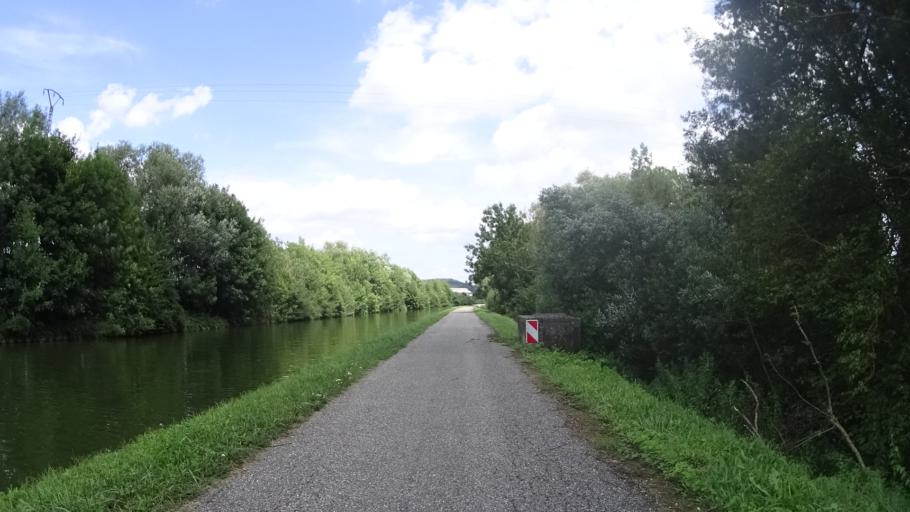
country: FR
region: Lorraine
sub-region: Departement de Meurthe-et-Moselle
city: Foug
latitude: 48.6764
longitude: 5.7931
